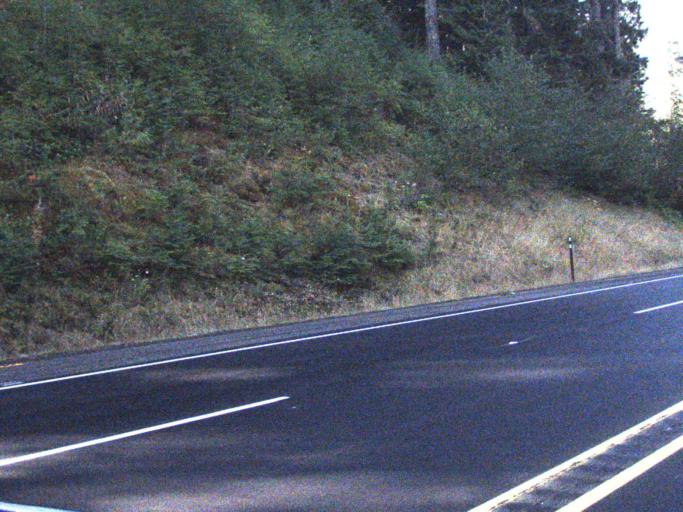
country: US
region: Washington
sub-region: Pierce County
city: Buckley
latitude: 46.6912
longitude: -121.5744
